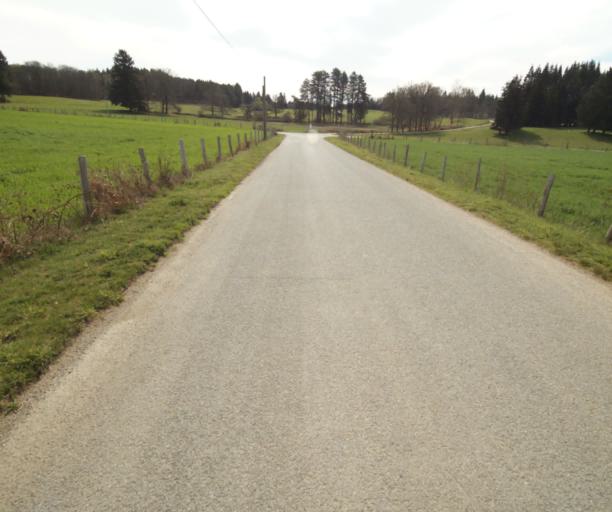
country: FR
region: Limousin
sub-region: Departement de la Correze
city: Correze
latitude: 45.3483
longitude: 1.8935
